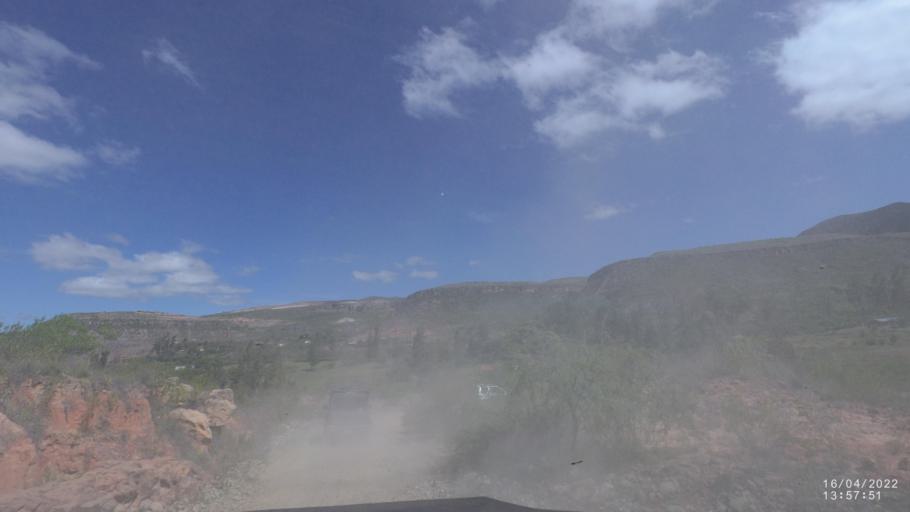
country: BO
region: Cochabamba
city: Mizque
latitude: -18.0388
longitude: -65.5588
